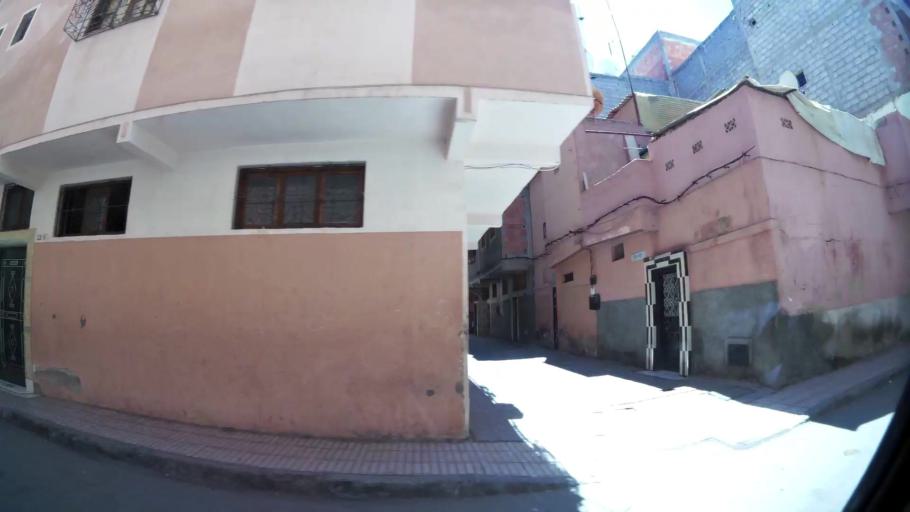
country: MA
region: Marrakech-Tensift-Al Haouz
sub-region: Marrakech
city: Marrakesh
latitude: 31.6576
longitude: -7.9929
